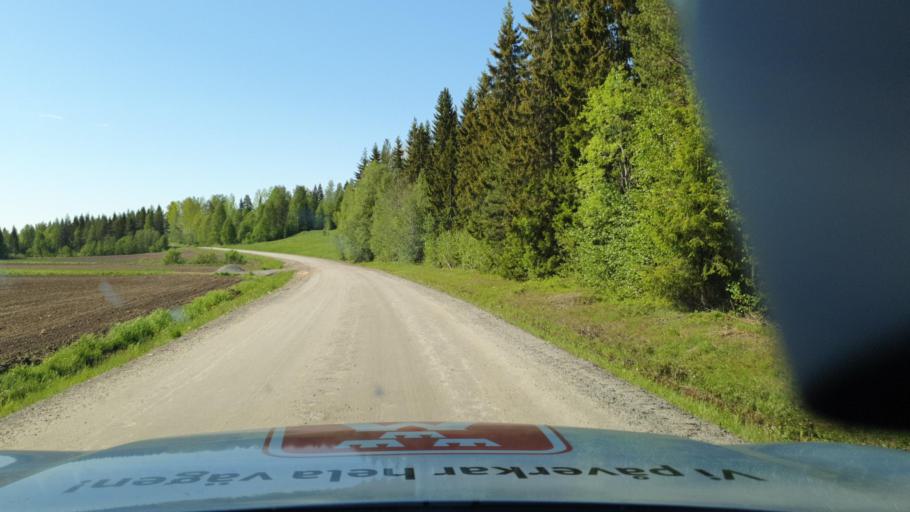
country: SE
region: Vaesterbotten
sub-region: Vannas Kommun
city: Vaennaes
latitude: 64.0048
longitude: 19.7266
